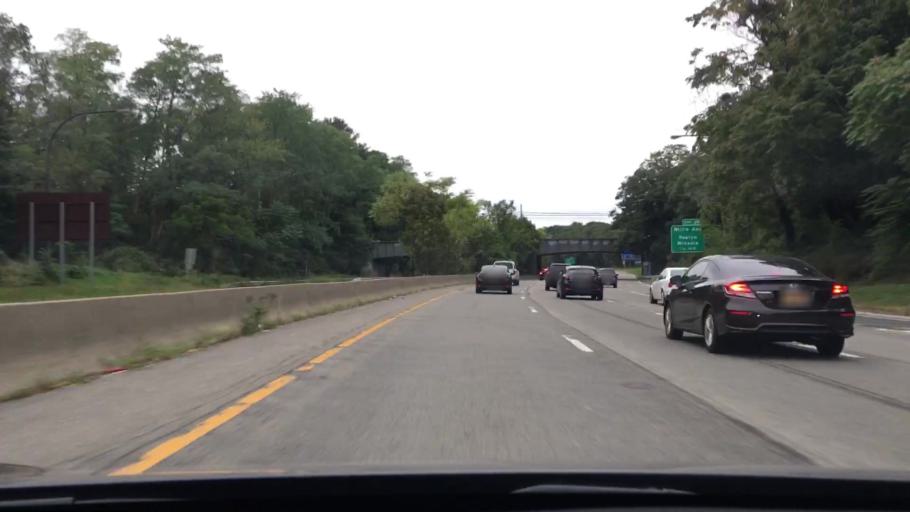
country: US
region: New York
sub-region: Nassau County
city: Albertson
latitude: 40.7812
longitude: -73.6416
